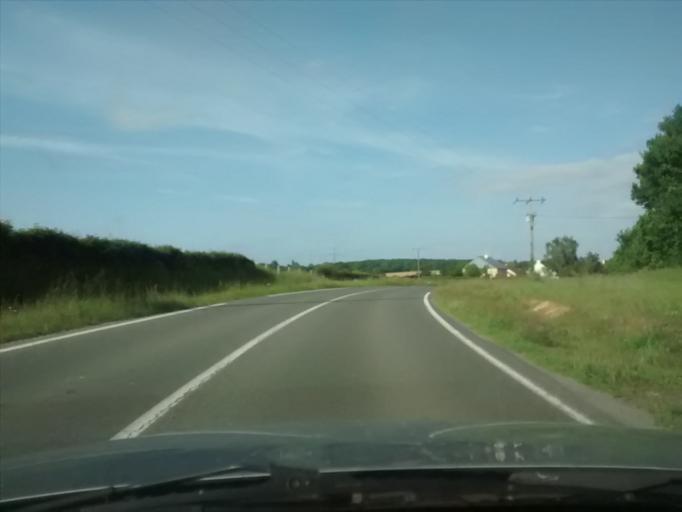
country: FR
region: Pays de la Loire
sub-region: Departement de la Mayenne
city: Entrammes
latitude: 47.9229
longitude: -0.6879
